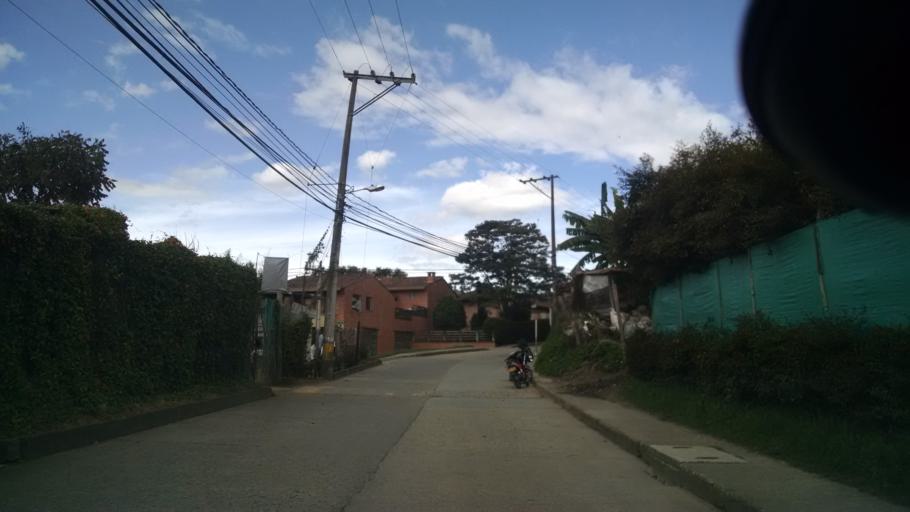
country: CO
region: Antioquia
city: El Retiro
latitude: 6.0563
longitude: -75.5061
